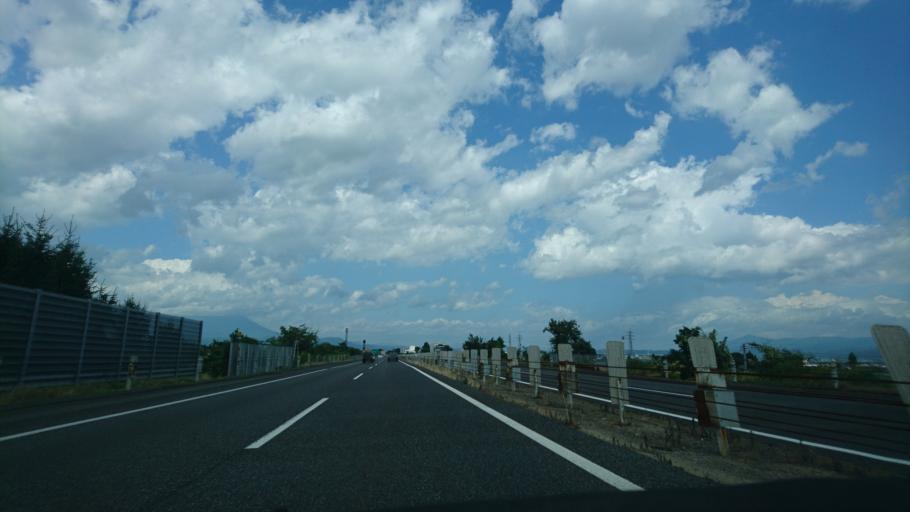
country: JP
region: Iwate
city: Morioka-shi
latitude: 39.6407
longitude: 141.1258
